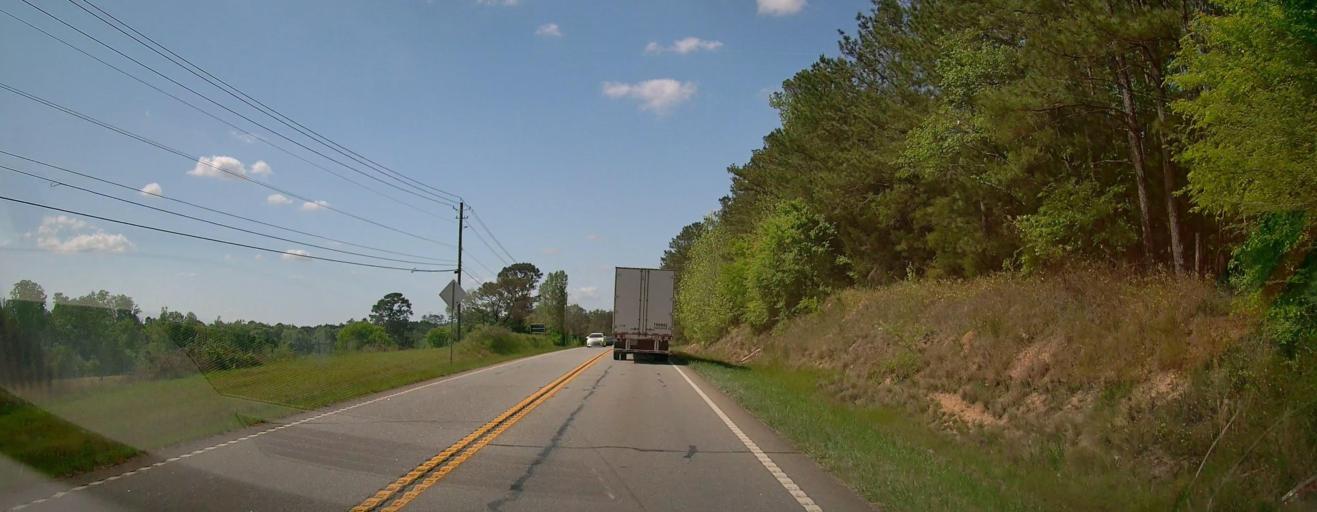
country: US
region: Georgia
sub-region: Greene County
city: Greensboro
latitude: 33.5031
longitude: -83.2234
